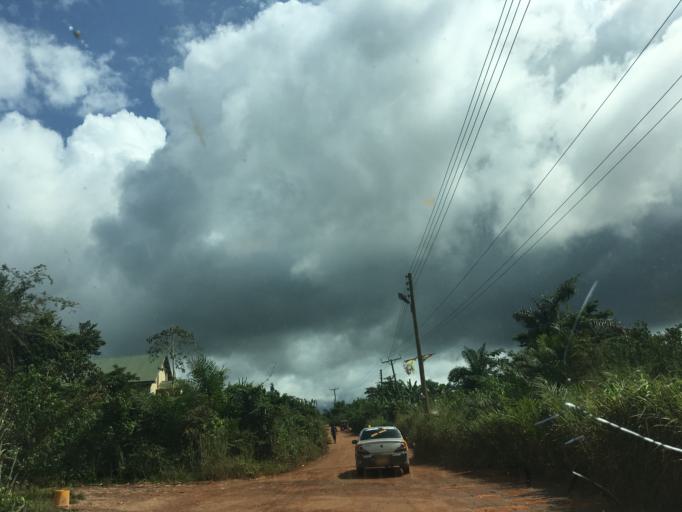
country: GH
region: Western
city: Wassa-Akropong
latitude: 5.7927
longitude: -2.4284
